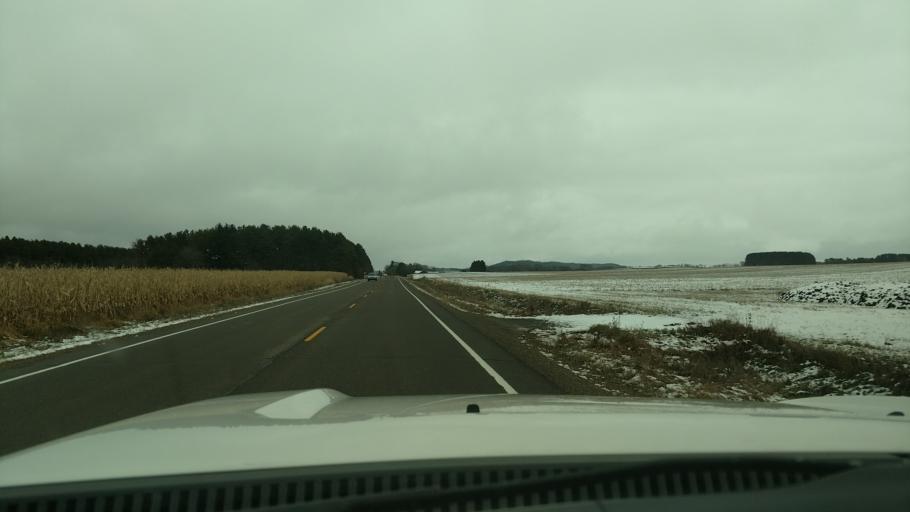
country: US
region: Wisconsin
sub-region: Dunn County
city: Colfax
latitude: 45.1426
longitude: -91.6745
